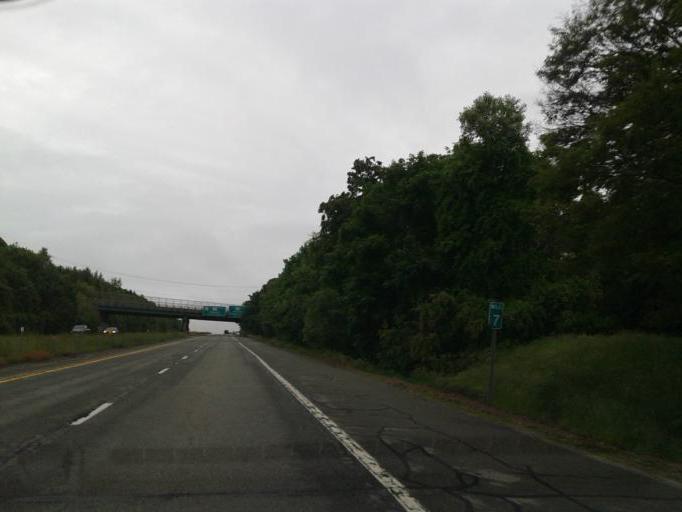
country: US
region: Rhode Island
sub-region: Newport County
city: Portsmouth
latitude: 41.6184
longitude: -71.2523
